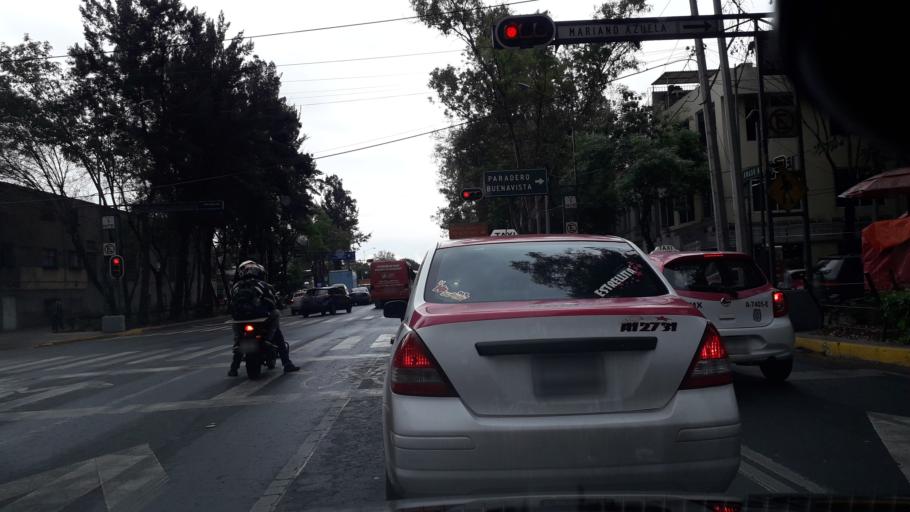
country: MX
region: Mexico City
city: Cuauhtemoc
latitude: 19.4465
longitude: -99.1547
